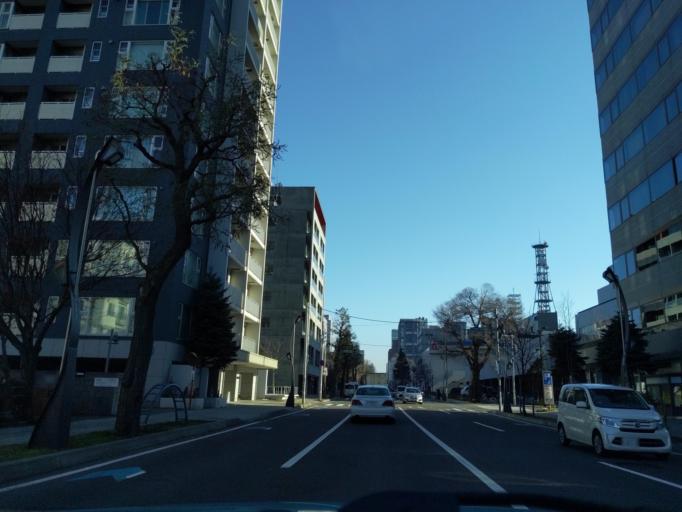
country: JP
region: Hokkaido
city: Sapporo
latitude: 43.0618
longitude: 141.3414
